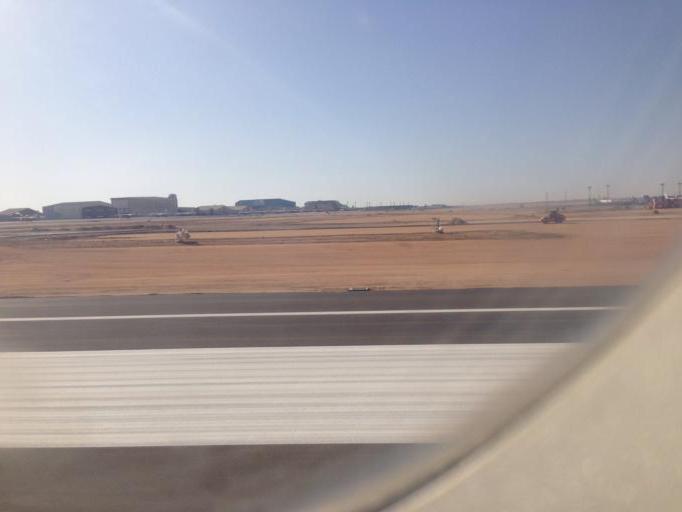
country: EG
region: Muhafazat al Qalyubiyah
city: Al Khankah
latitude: 30.1367
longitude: 31.4029
